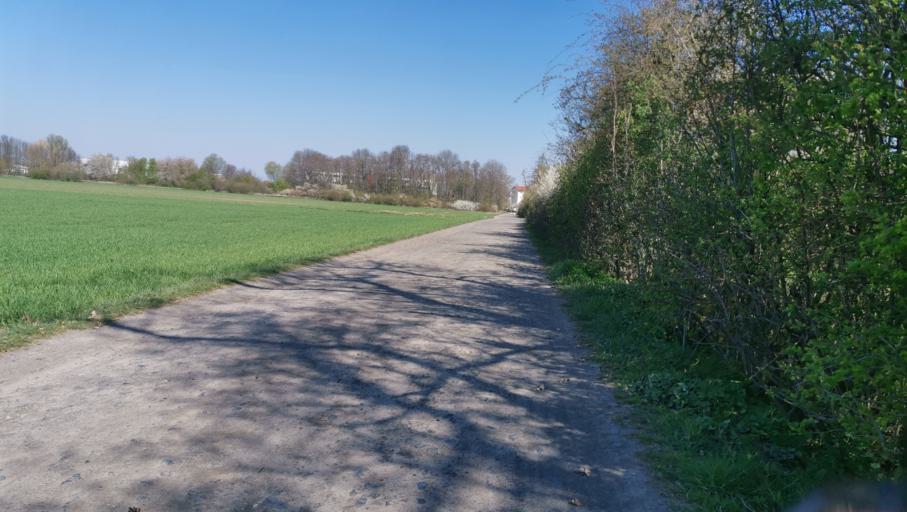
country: DE
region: Hesse
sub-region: Regierungsbezirk Darmstadt
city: Karben
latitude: 50.2184
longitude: 8.7612
